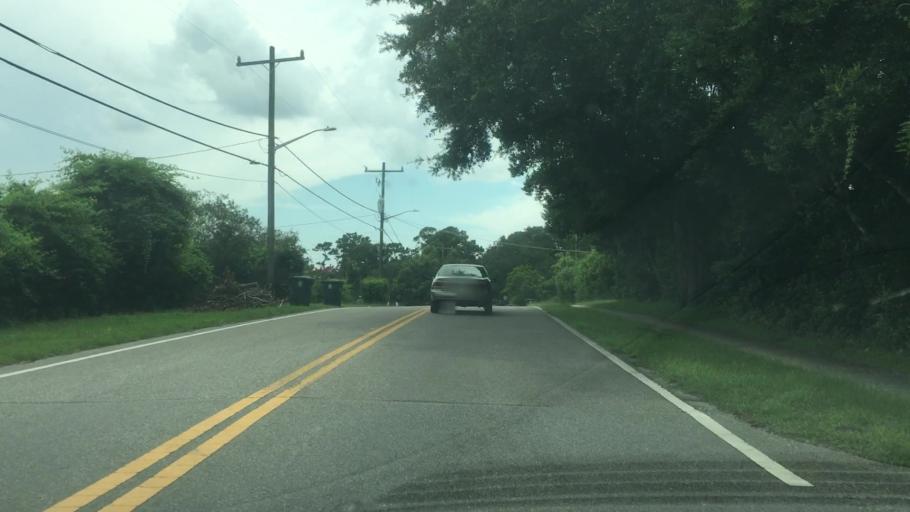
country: US
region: Florida
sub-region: Duval County
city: Jacksonville
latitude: 30.3129
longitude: -81.5473
